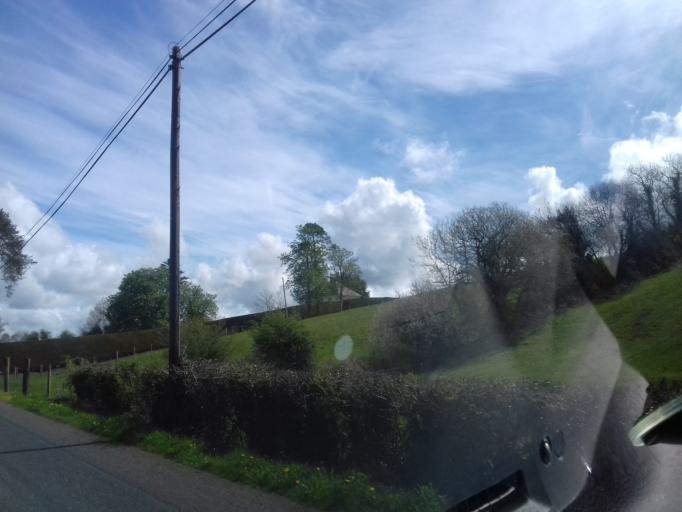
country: IE
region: Ulster
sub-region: An Cabhan
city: Ballyconnell
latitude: 54.1569
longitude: -7.5225
